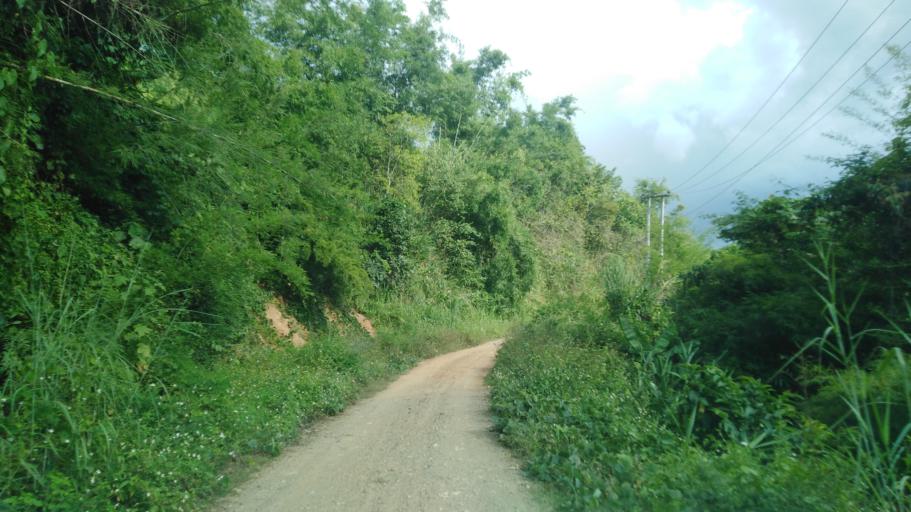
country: TH
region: Chiang Rai
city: Wiang Kaen
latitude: 19.7863
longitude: 100.6424
